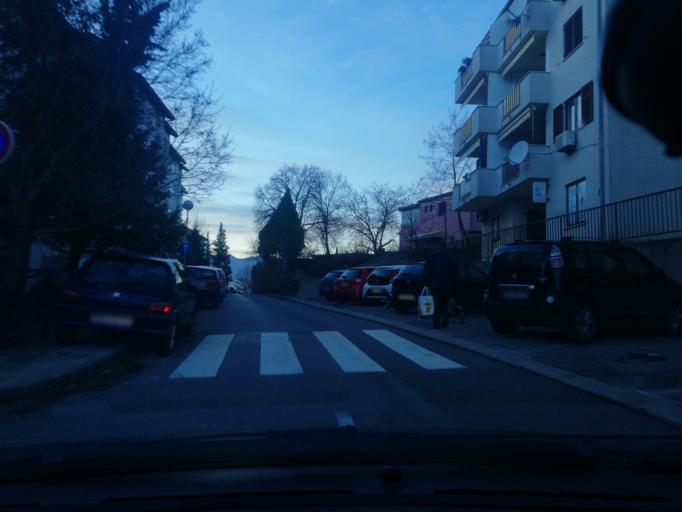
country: HR
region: Primorsko-Goranska
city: Marinici
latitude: 45.3532
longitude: 14.3718
